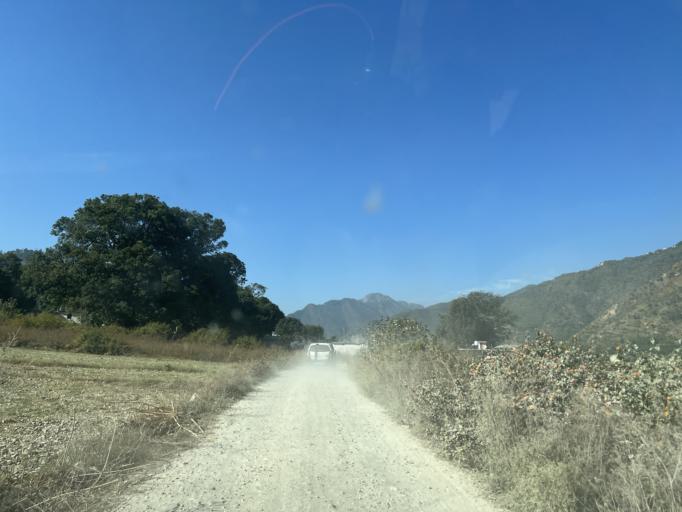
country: IN
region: Uttarakhand
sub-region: Almora
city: Ranikhet
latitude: 29.5518
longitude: 79.3889
